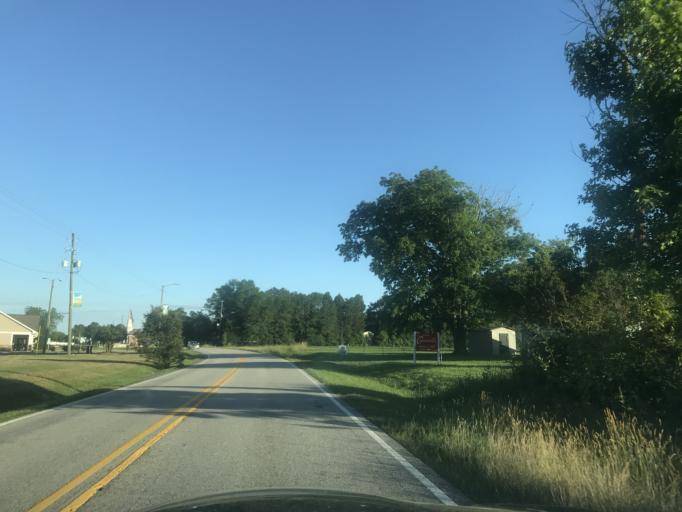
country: US
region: North Carolina
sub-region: Johnston County
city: Archer Lodge
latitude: 35.6966
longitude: -78.3775
